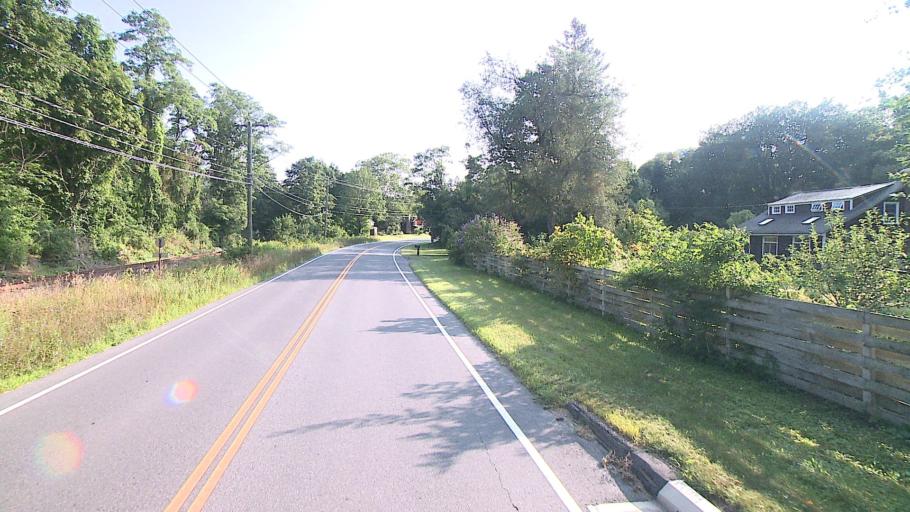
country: US
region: Connecticut
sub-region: Litchfield County
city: Kent
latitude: 41.7381
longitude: -73.4685
